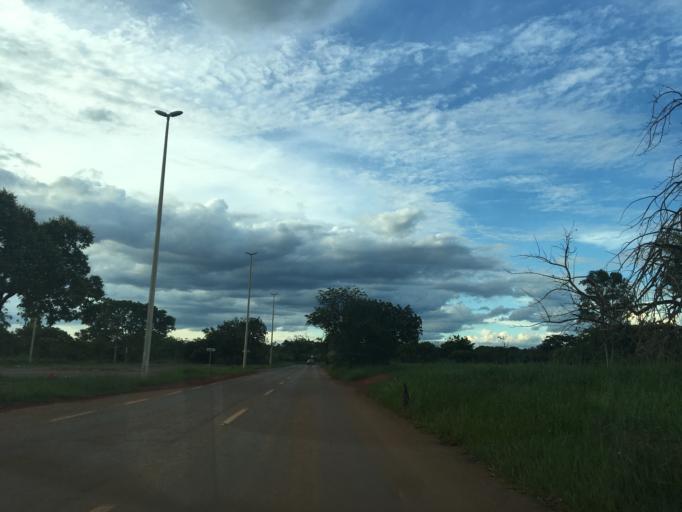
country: BR
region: Federal District
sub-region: Brasilia
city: Brasilia
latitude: -15.8299
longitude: -47.9437
